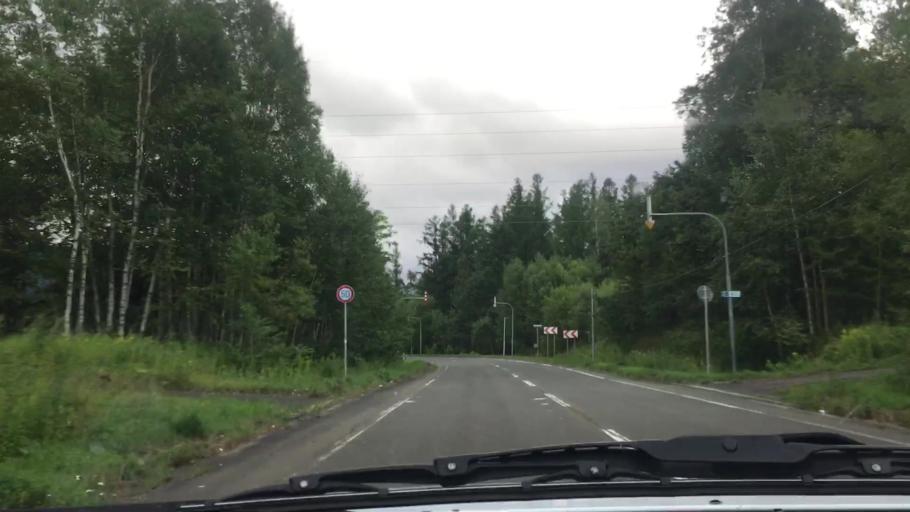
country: JP
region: Hokkaido
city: Shimo-furano
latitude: 43.0553
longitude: 142.6685
